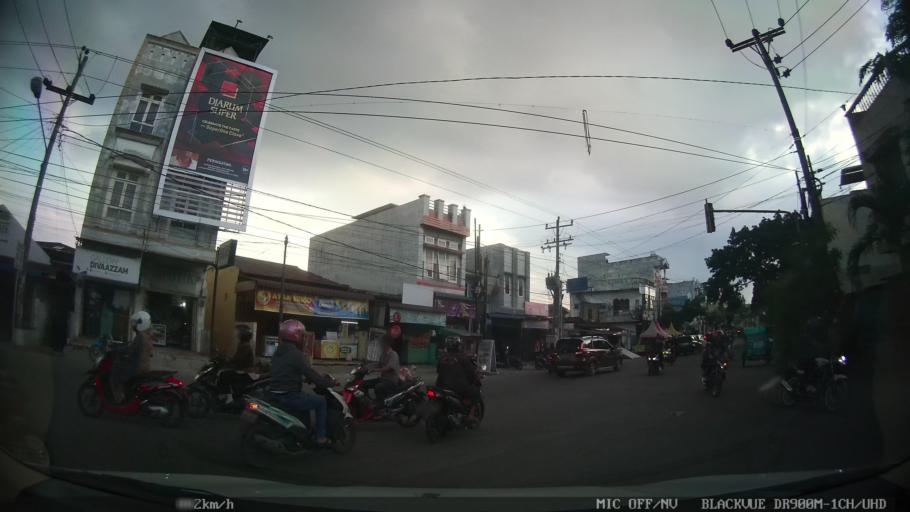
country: ID
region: North Sumatra
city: Medan
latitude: 3.5820
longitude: 98.7111
